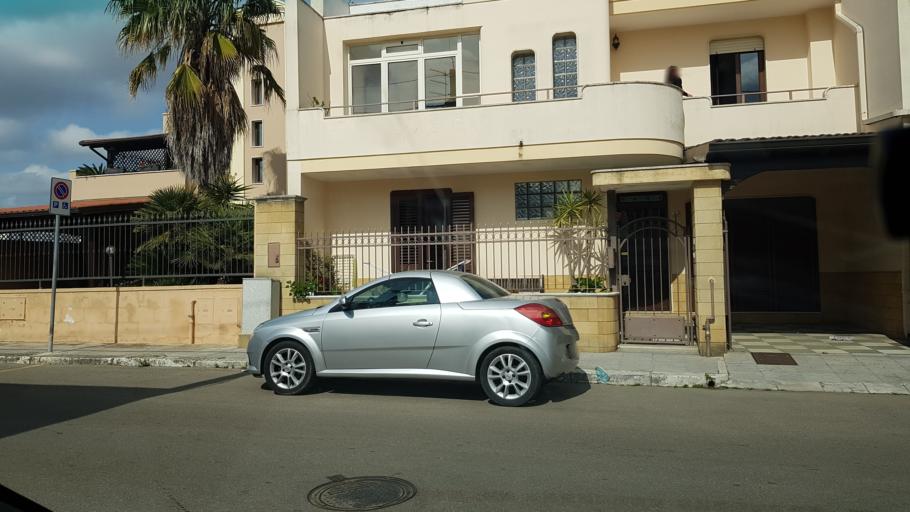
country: IT
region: Apulia
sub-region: Provincia di Lecce
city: Squinzano
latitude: 40.4303
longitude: 18.0498
